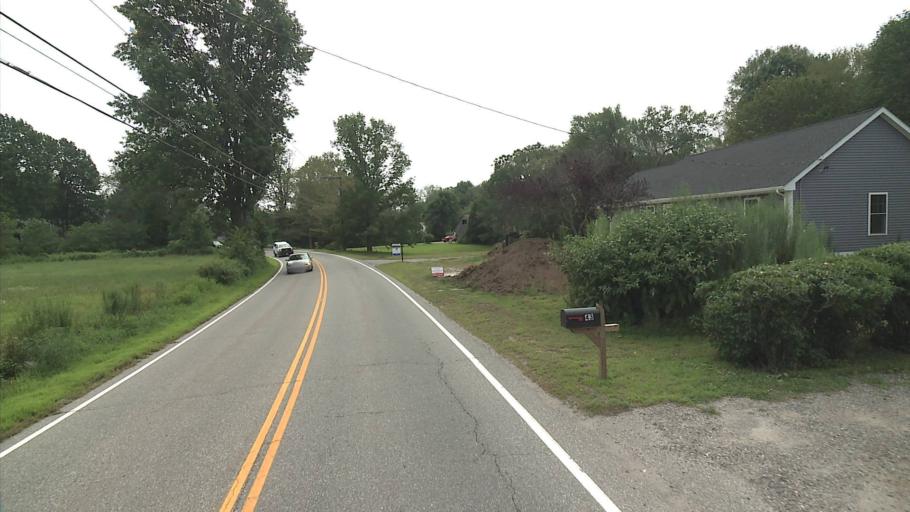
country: US
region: Connecticut
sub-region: Windham County
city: East Brooklyn
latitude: 41.7813
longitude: -71.9495
